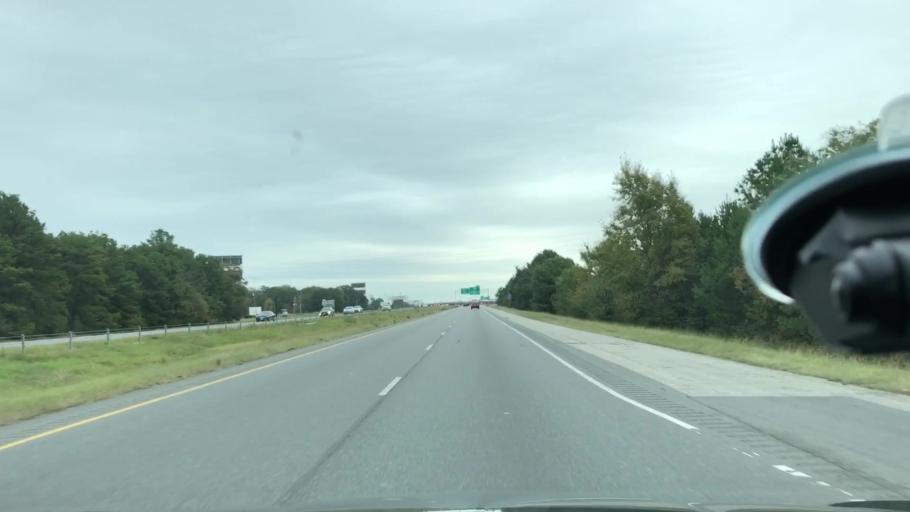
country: US
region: Arkansas
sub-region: Miller County
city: Texarkana
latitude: 33.4769
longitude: -94.0014
